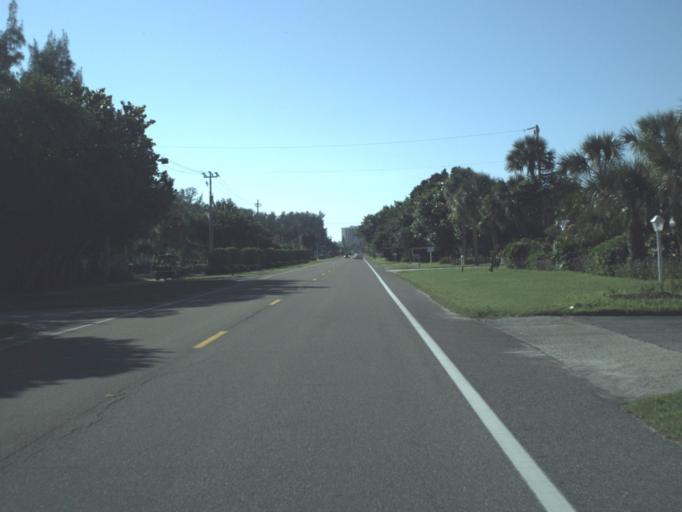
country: US
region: Florida
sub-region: Manatee County
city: Longboat Key
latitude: 27.3770
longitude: -82.6338
